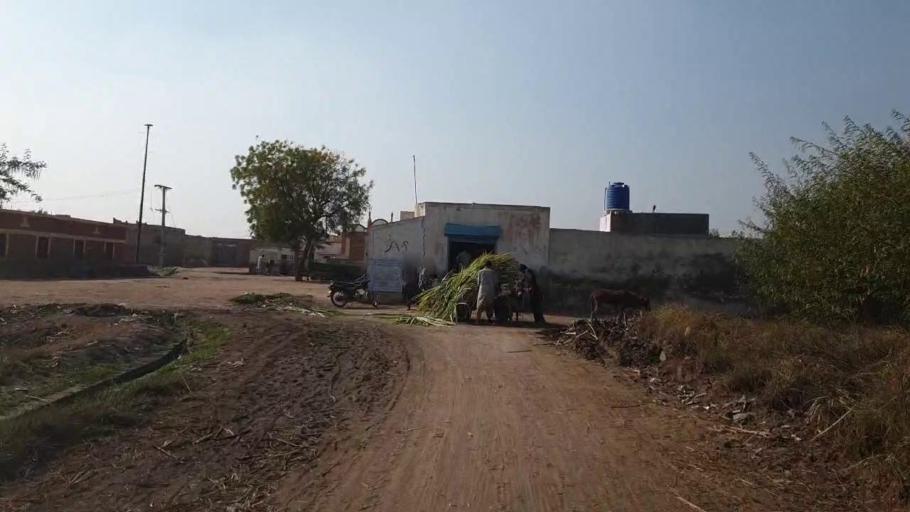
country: PK
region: Sindh
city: Tando Adam
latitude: 25.6653
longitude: 68.5713
